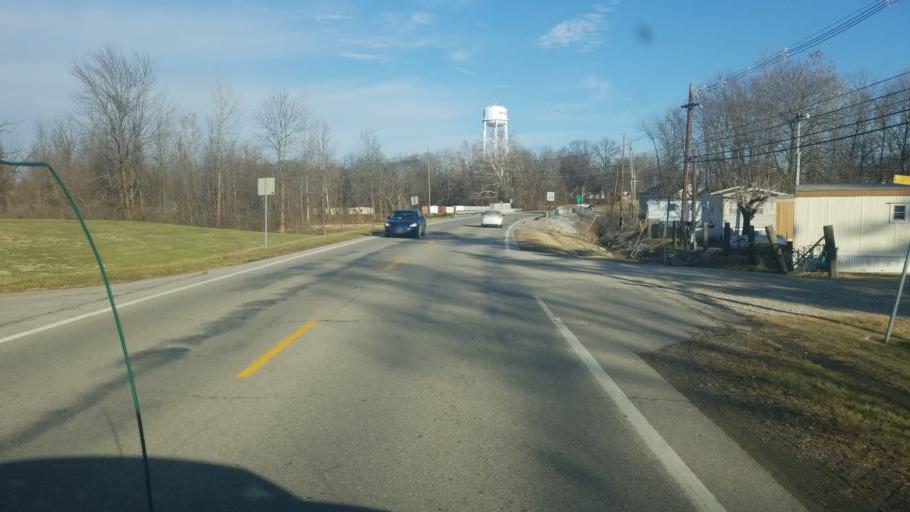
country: US
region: Illinois
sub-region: Wabash County
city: Mount Carmel
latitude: 38.4027
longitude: -87.7807
